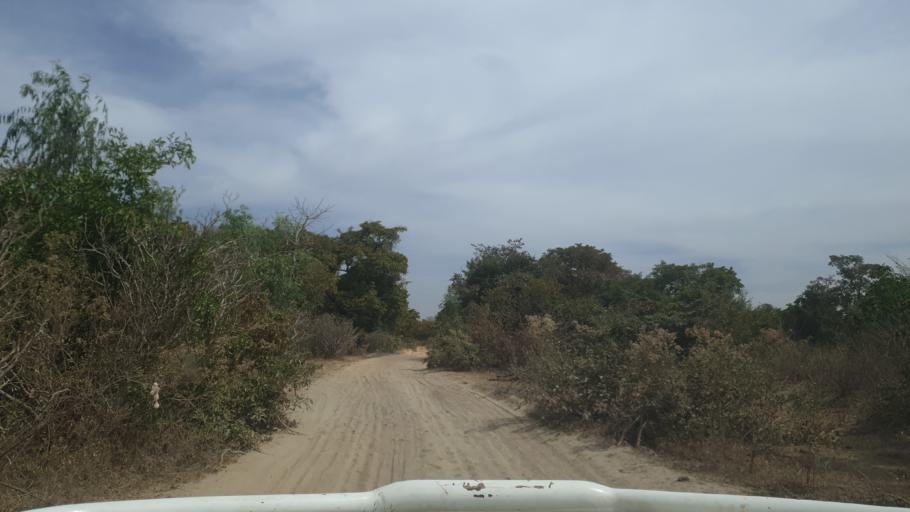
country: ML
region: Sikasso
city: Yorosso
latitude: 12.2423
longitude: -4.7326
